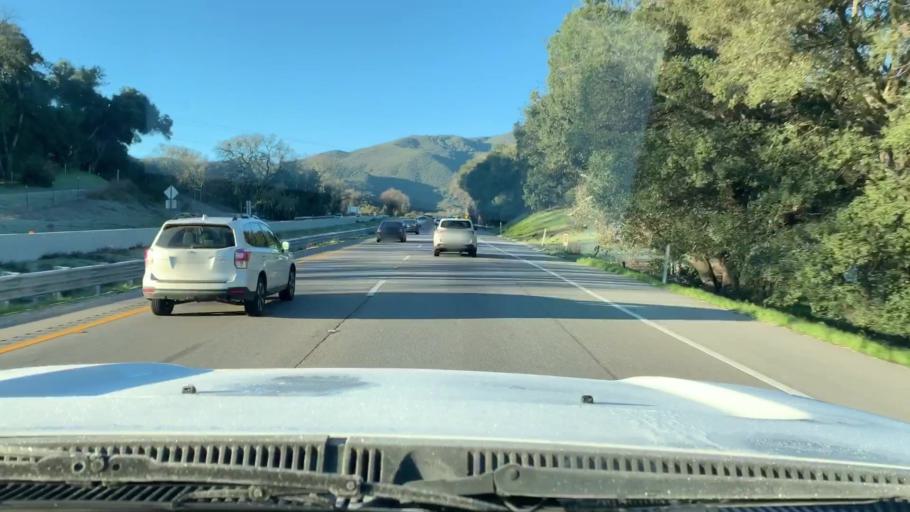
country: US
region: California
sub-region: San Luis Obispo County
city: Santa Margarita
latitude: 35.3784
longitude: -120.6355
